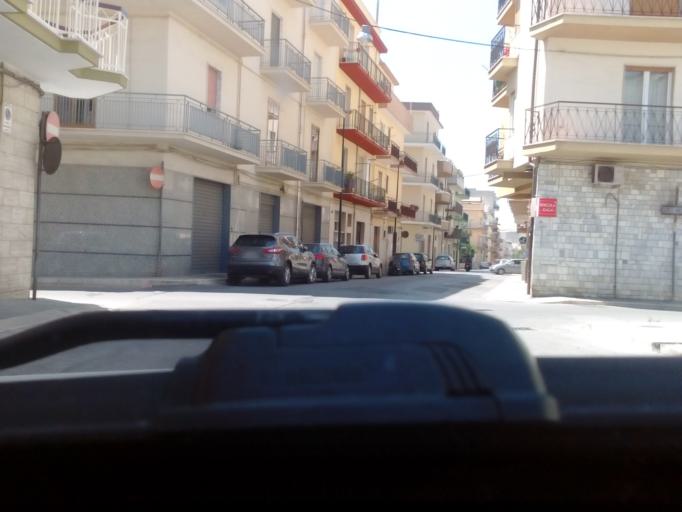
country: IT
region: Apulia
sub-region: Provincia di Bari
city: Gravina in Puglia
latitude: 40.8207
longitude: 16.4220
